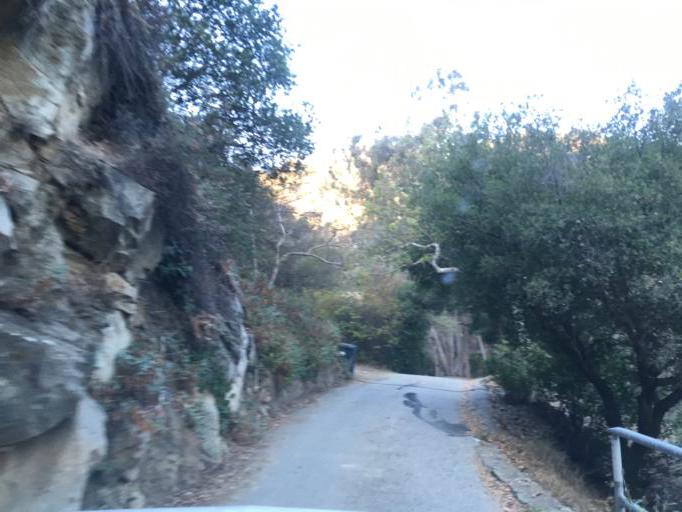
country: US
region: California
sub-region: Los Angeles County
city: Las Flores
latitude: 34.0545
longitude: -118.6385
